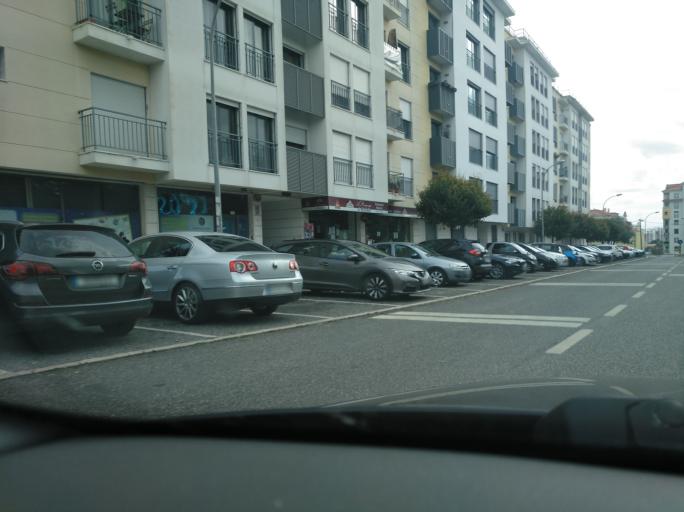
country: PT
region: Lisbon
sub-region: Amadora
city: Amadora
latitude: 38.7458
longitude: -9.2273
